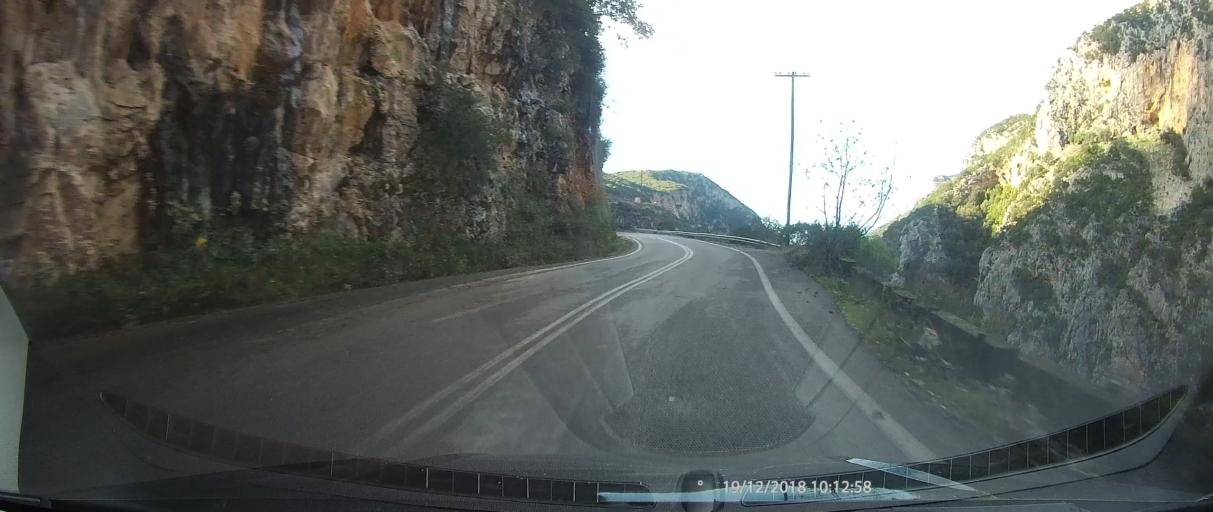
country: GR
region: Peloponnese
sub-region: Nomos Messinias
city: Kalamata
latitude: 37.0881
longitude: 22.1628
